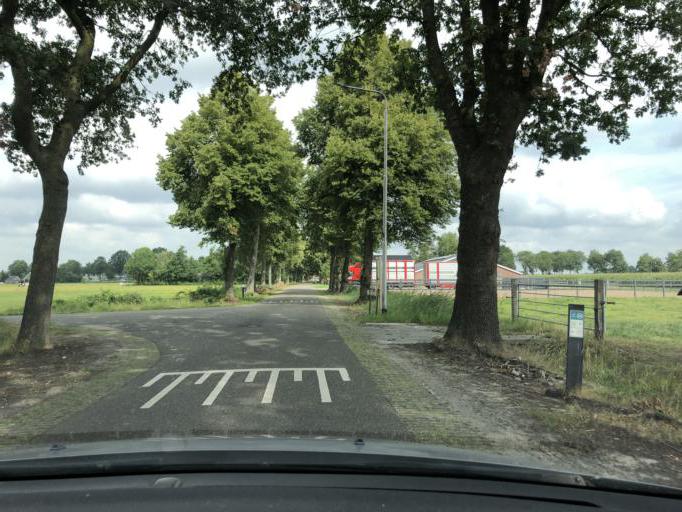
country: NL
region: Overijssel
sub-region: Gemeente Dalfsen
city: Dalfsen
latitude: 52.5885
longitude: 6.2932
